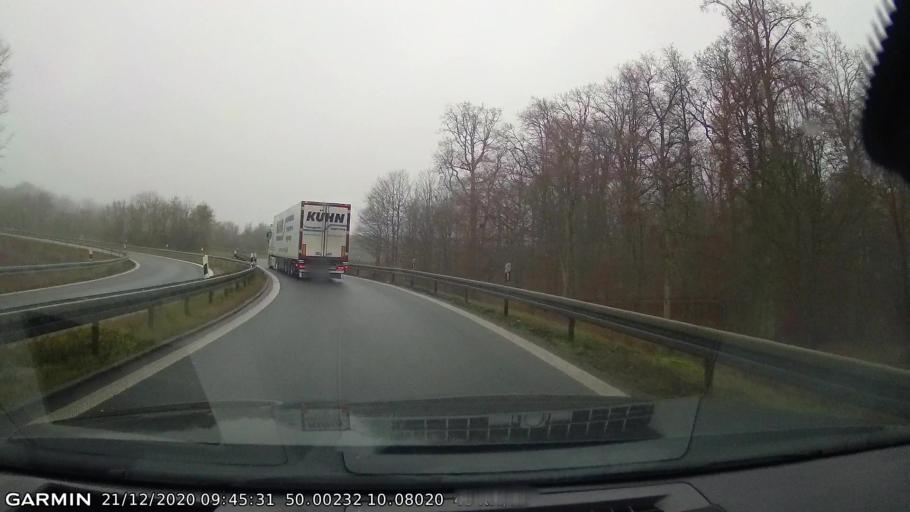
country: DE
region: Bavaria
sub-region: Regierungsbezirk Unterfranken
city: Werneck
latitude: 50.0024
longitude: 10.0802
